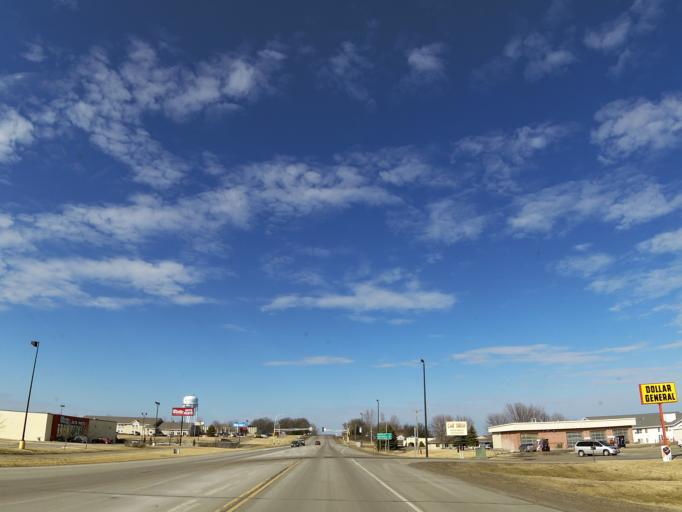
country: US
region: Minnesota
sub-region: Waseca County
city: Waseca
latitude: 44.0964
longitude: -93.5071
